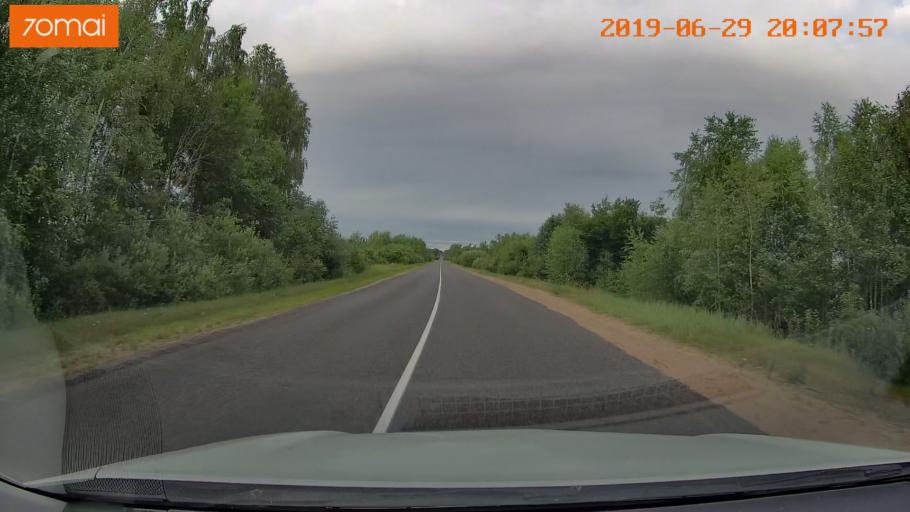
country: BY
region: Brest
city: Lahishyn
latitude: 52.3422
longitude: 26.0474
